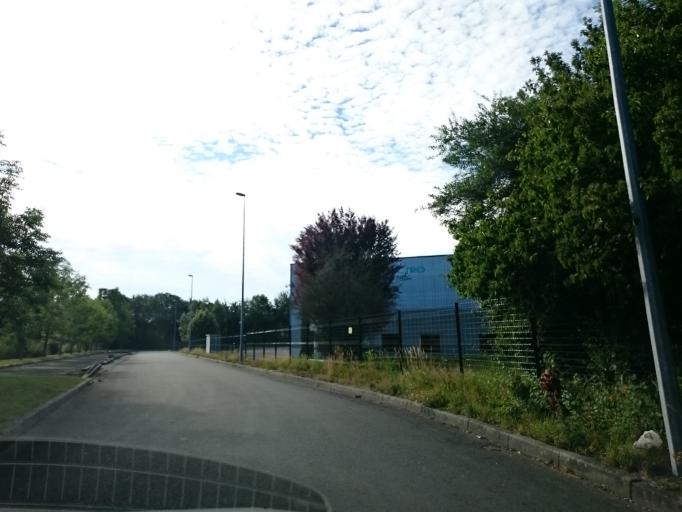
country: FR
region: Brittany
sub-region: Departement d'Ille-et-Vilaine
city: Chantepie
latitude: 48.0866
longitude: -1.6283
